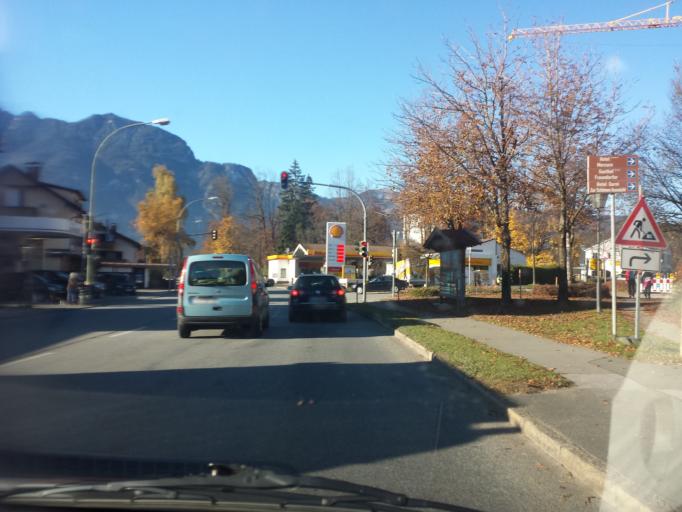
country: DE
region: Bavaria
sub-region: Upper Bavaria
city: Garmisch-Partenkirchen
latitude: 47.4894
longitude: 11.1136
